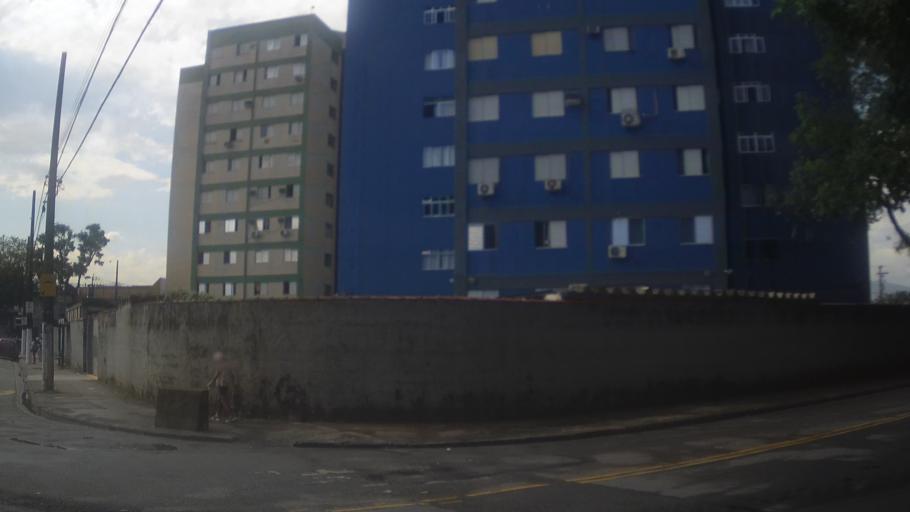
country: BR
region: Sao Paulo
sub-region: Santos
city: Santos
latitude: -23.9329
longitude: -46.3489
